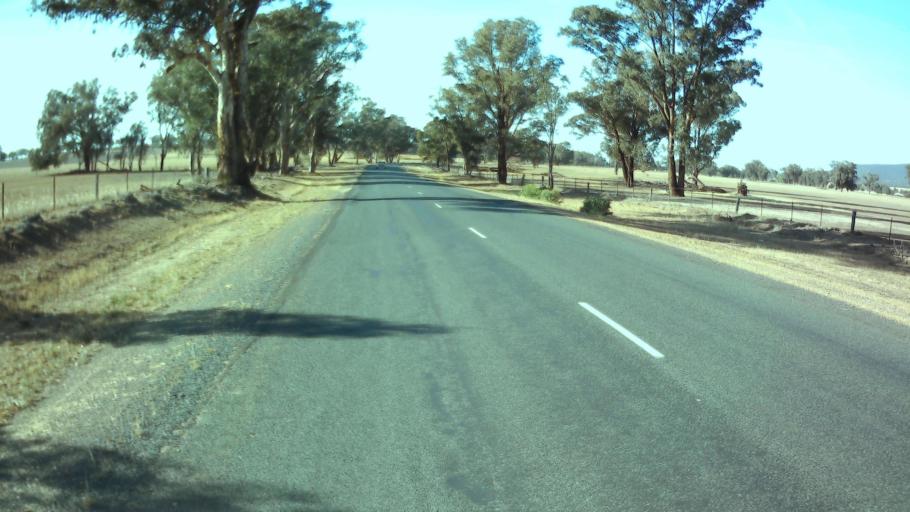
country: AU
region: New South Wales
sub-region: Weddin
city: Grenfell
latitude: -33.9325
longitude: 148.1375
